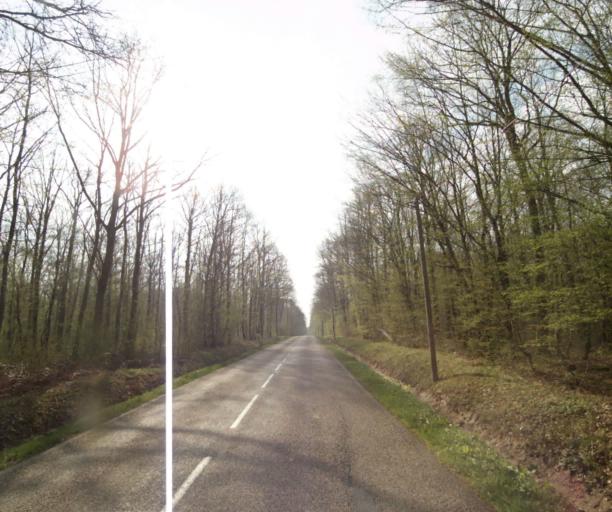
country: FR
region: Bourgogne
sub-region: Departement de Saone-et-Loire
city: Charolles
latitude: 46.4582
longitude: 4.2539
